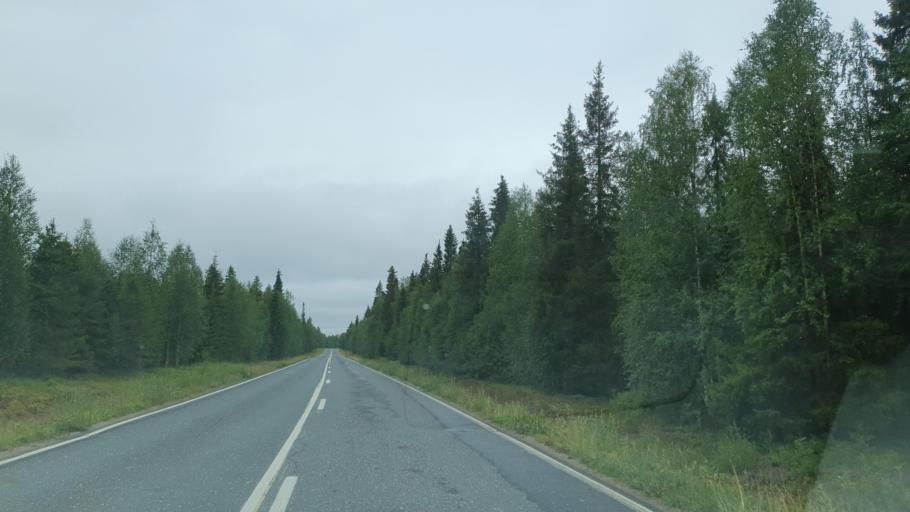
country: FI
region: Lapland
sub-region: Itae-Lappi
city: Pelkosenniemi
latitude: 67.2289
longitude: 27.3546
